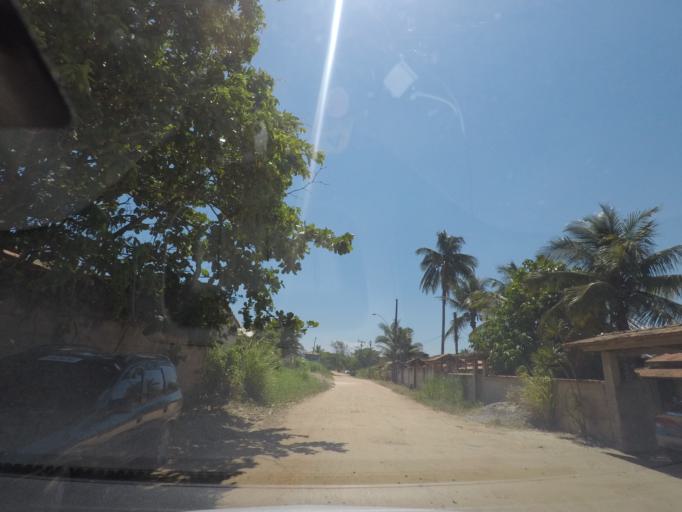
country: BR
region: Rio de Janeiro
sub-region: Marica
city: Marica
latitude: -22.9708
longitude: -42.9400
